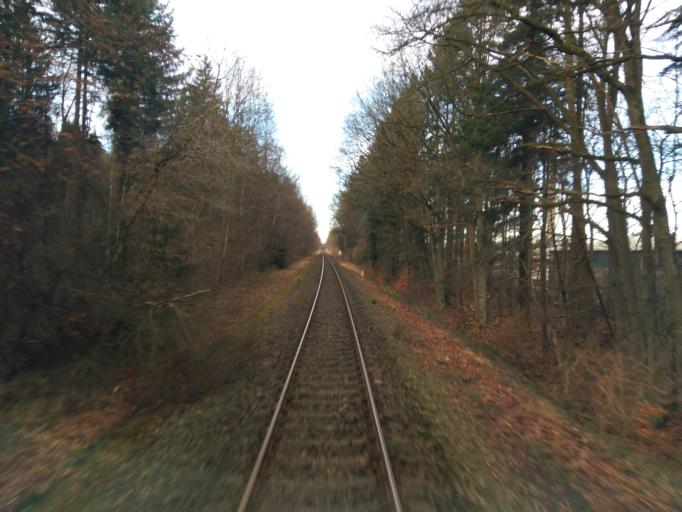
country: DE
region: Lower Saxony
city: Uelzen
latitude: 52.9889
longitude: 10.5365
